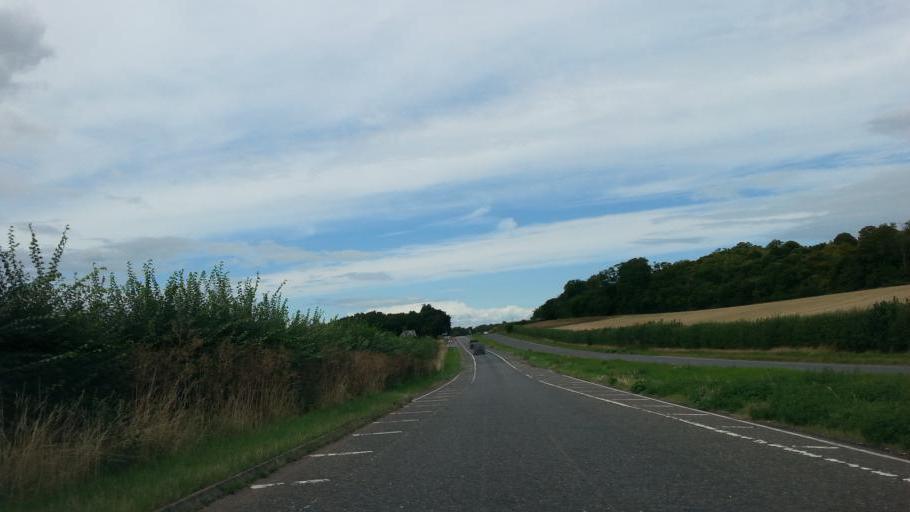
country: GB
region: England
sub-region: Cambridgeshire
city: Sawston
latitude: 52.1308
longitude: 0.2181
